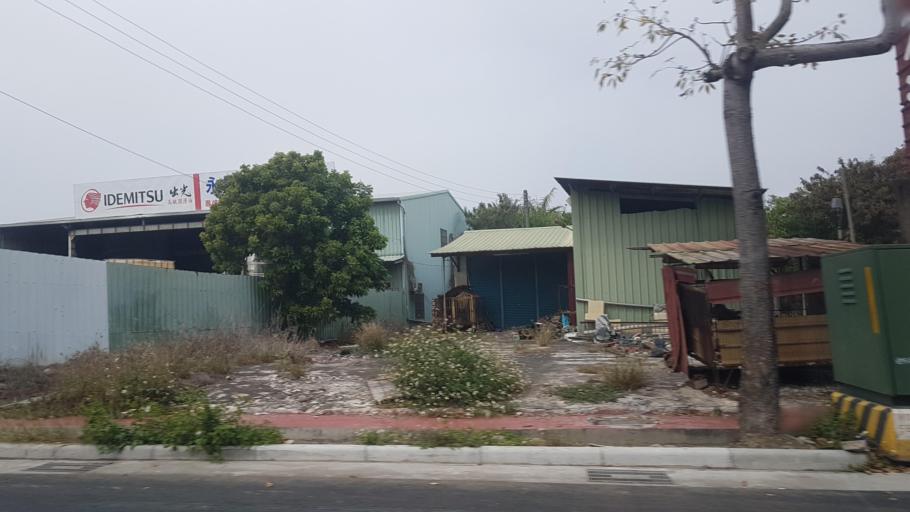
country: TW
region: Taiwan
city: Xinying
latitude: 23.3141
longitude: 120.3007
